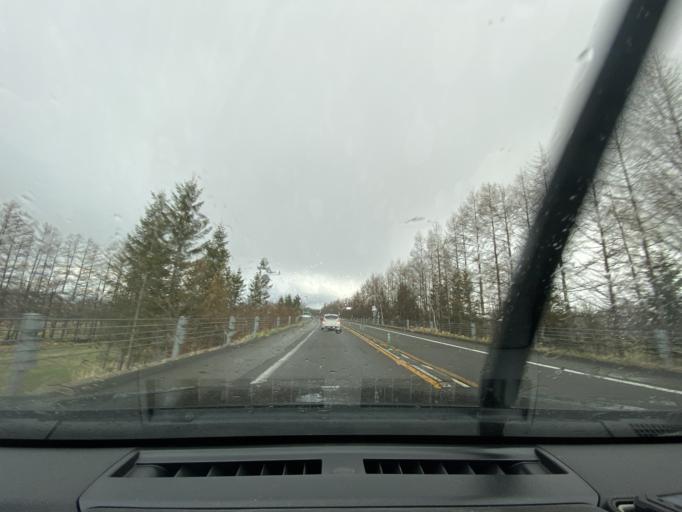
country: JP
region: Hokkaido
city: Otofuke
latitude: 42.9736
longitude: 142.8814
